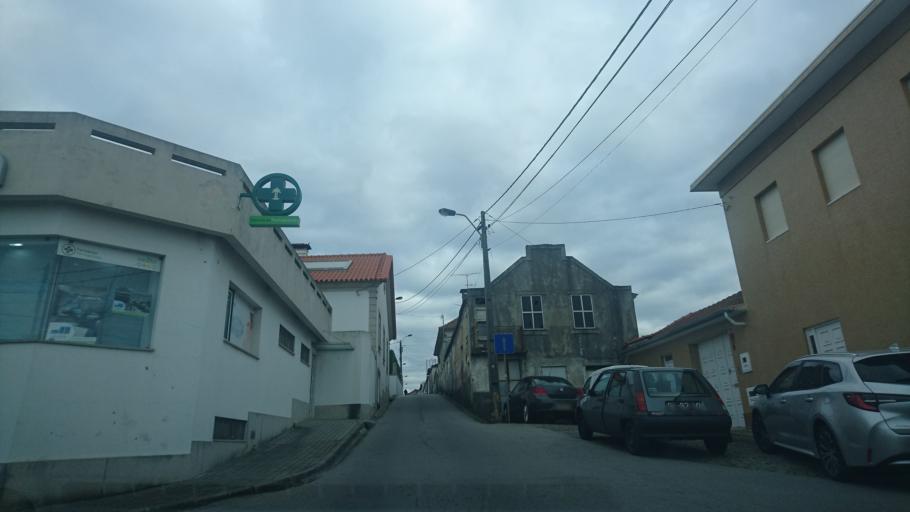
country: PT
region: Aveiro
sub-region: Ovar
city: Esmoriz
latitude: 40.9555
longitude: -8.6232
